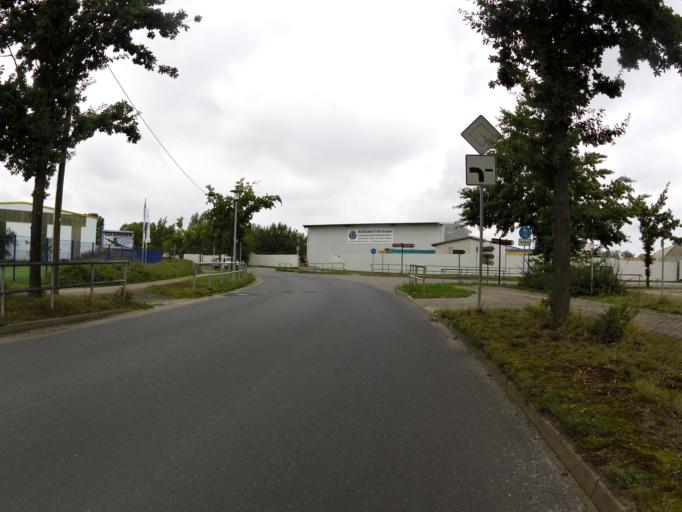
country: DE
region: Brandenburg
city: Storkow
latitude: 52.2694
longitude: 13.9400
